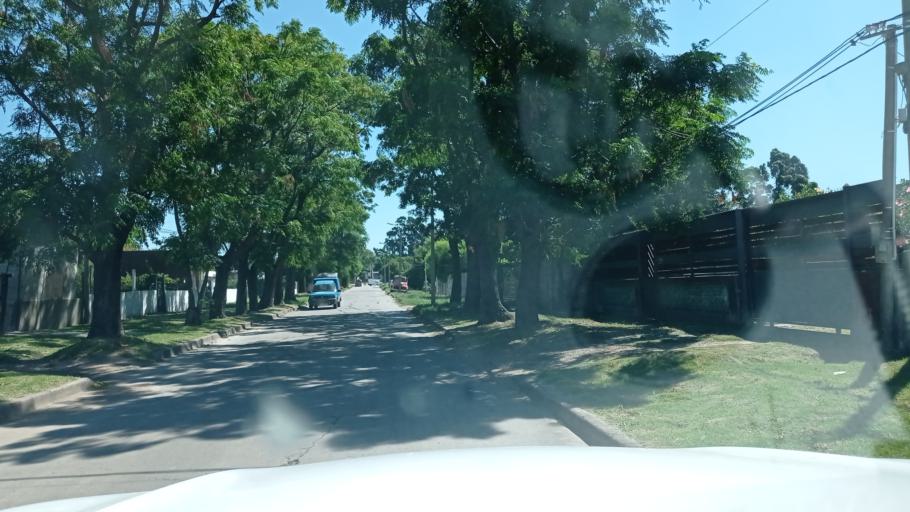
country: UY
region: Montevideo
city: Montevideo
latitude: -34.8663
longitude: -56.2661
